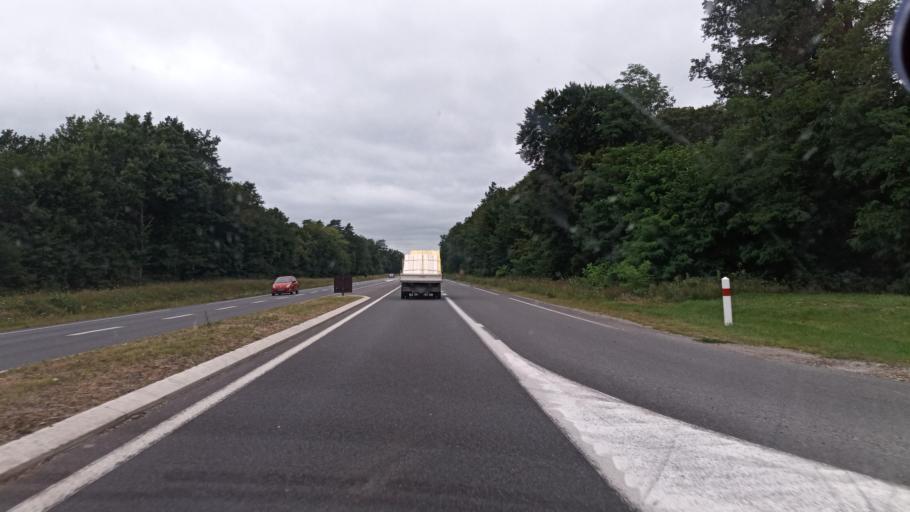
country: FR
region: Ile-de-France
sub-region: Departement de Seine-et-Marne
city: Avon
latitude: 48.3966
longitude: 2.7106
